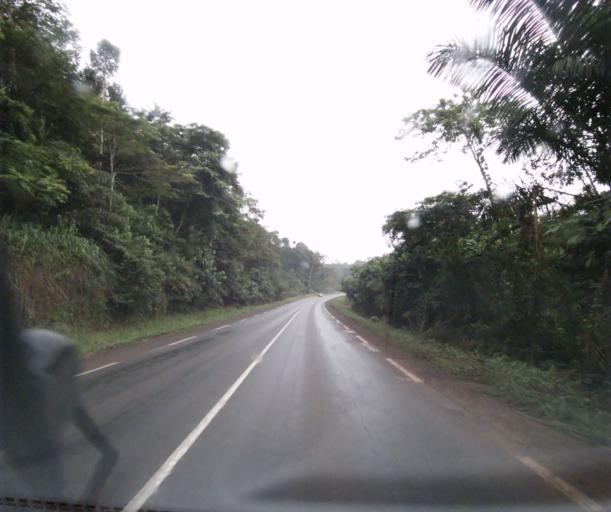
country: CM
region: Centre
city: Mbankomo
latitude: 3.7643
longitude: 11.1951
